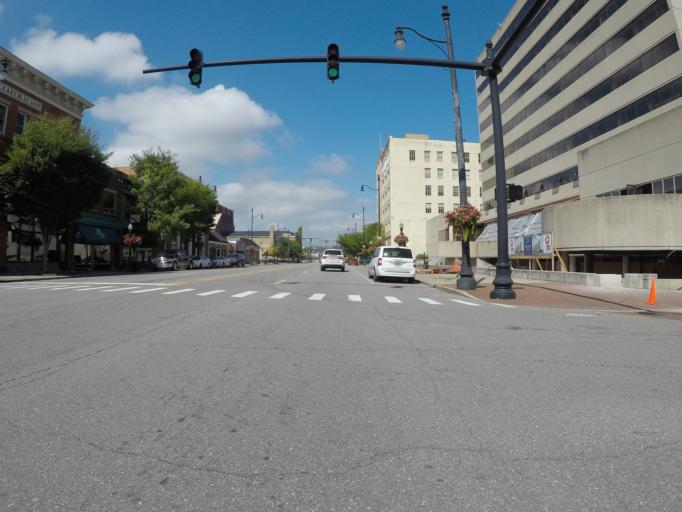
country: US
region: Kentucky
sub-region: Boyd County
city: Ashland
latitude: 38.4793
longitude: -82.6408
